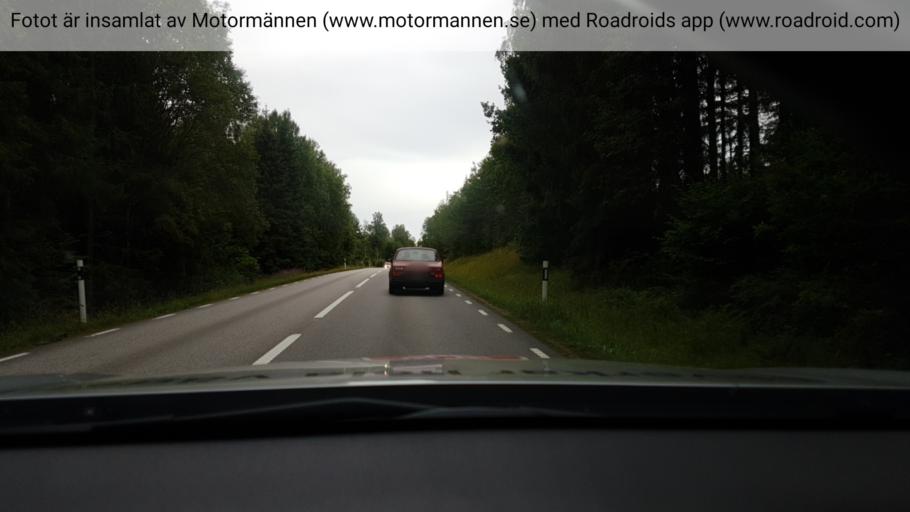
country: SE
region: Vaestra Goetaland
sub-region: Bengtsfors Kommun
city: Billingsfors
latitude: 58.9110
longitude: 12.2205
